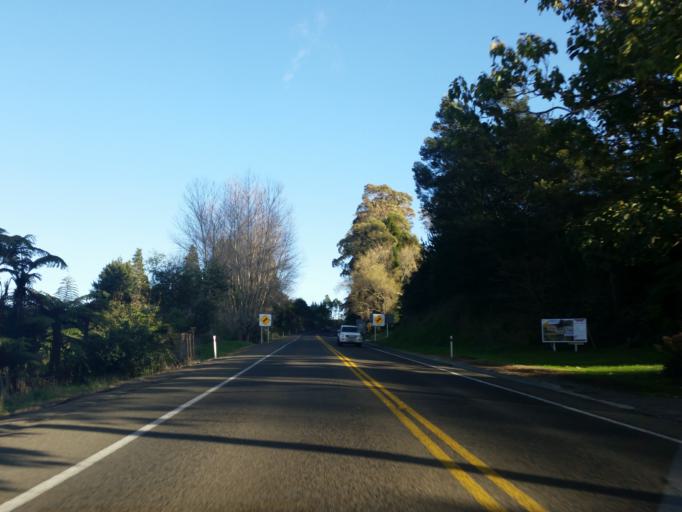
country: NZ
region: Bay of Plenty
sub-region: Tauranga City
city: Tauranga
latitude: -37.6830
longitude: 176.0300
